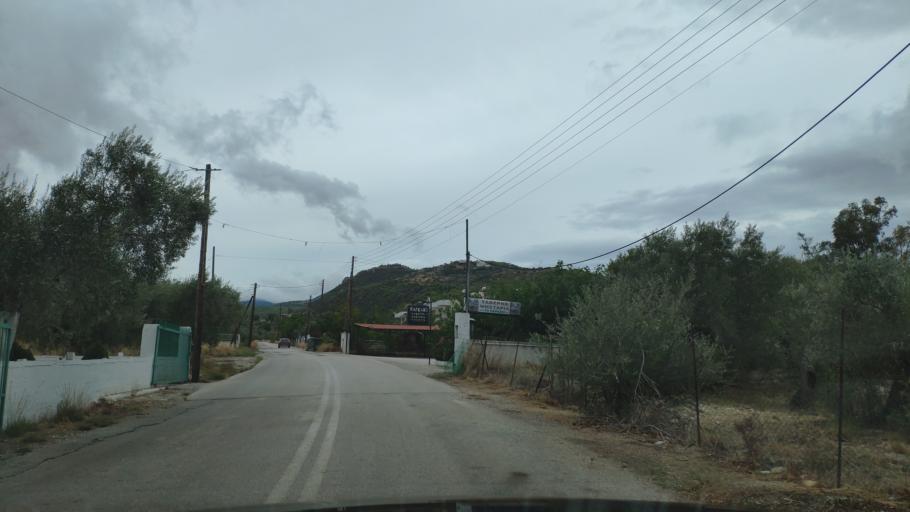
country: GR
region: Peloponnese
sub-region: Nomos Korinthias
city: Perachora
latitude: 38.0321
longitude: 22.8961
